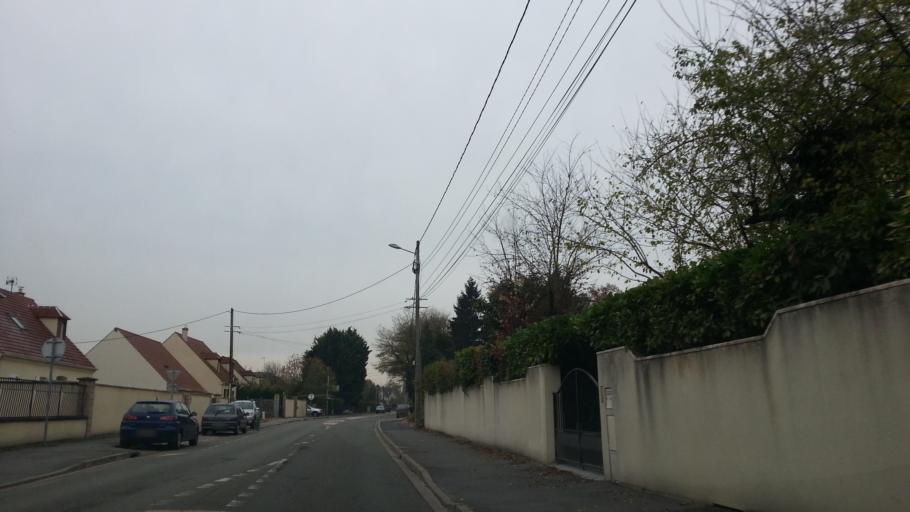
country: FR
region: Picardie
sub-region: Departement de l'Oise
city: Villers-sous-Saint-Leu
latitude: 49.2134
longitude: 2.4039
